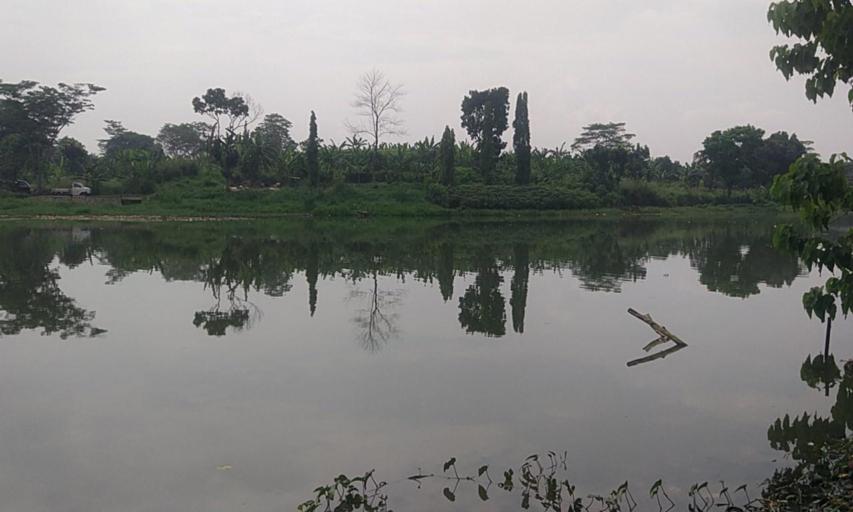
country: ID
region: West Java
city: Ciampea
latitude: -6.4960
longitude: 106.7448
